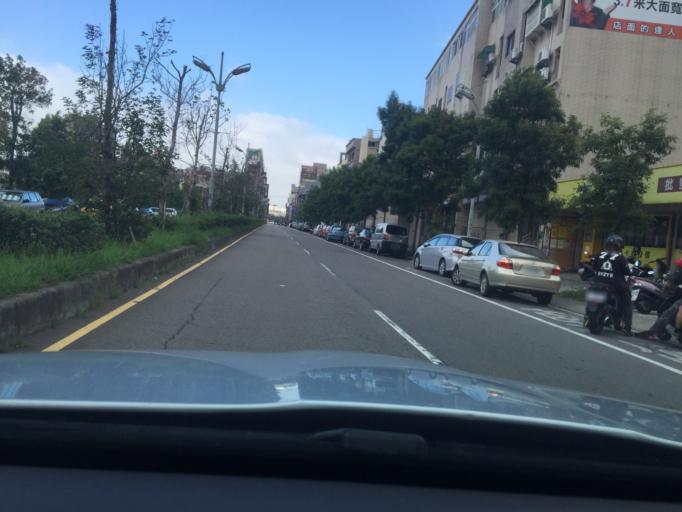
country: TW
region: Taiwan
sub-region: Hsinchu
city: Zhubei
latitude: 24.8227
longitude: 121.0072
